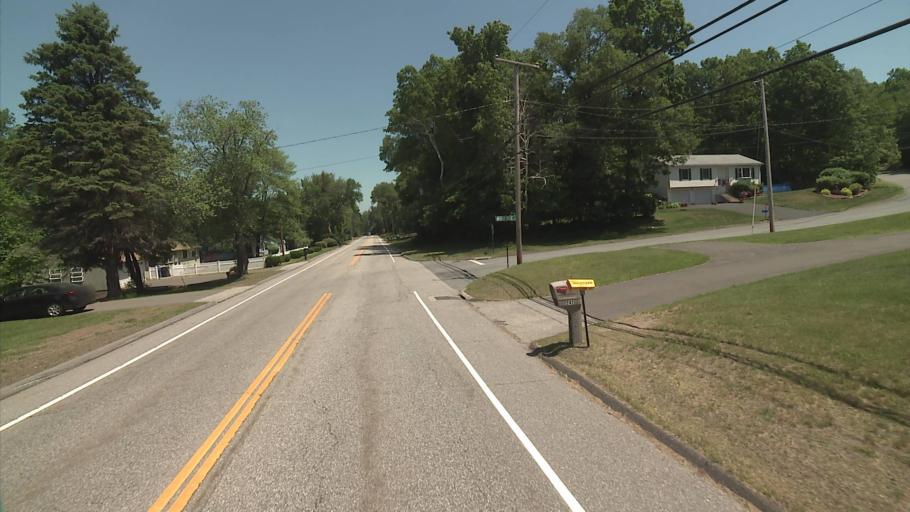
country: US
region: Connecticut
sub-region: Tolland County
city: Tolland
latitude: 41.8871
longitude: -72.4006
